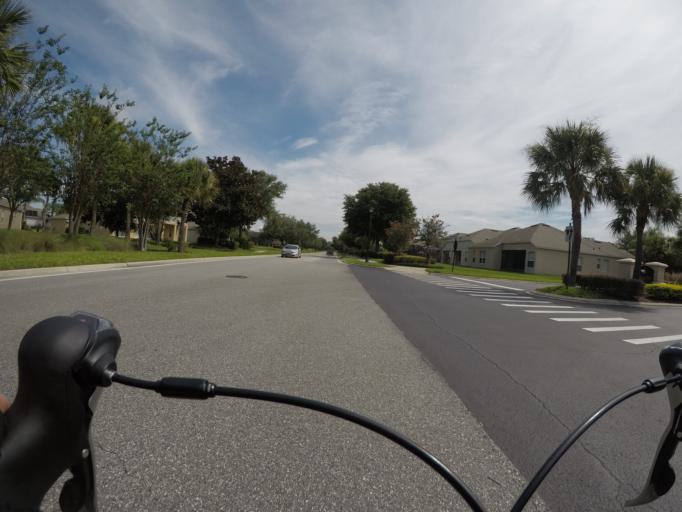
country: US
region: Florida
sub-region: Orange County
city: Taft
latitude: 28.4042
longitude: -81.2210
